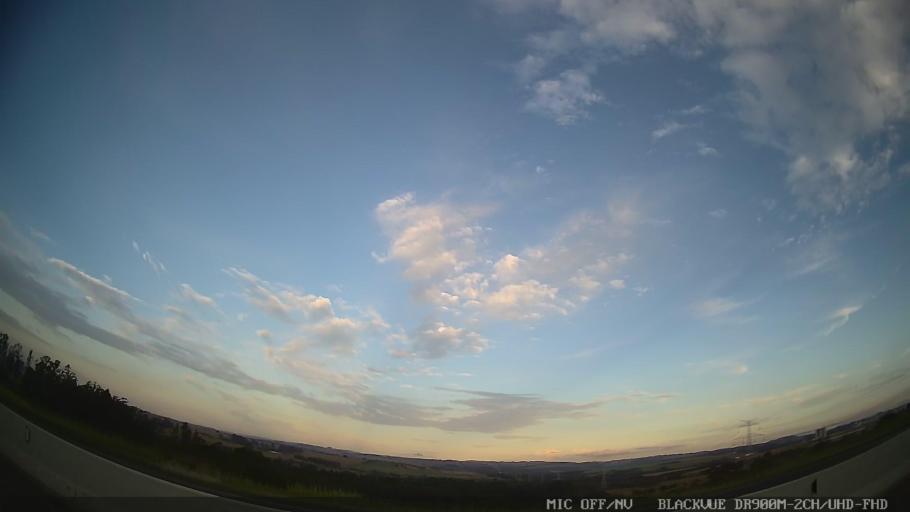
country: BR
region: Sao Paulo
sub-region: Salto
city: Salto
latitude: -23.1613
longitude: -47.2636
